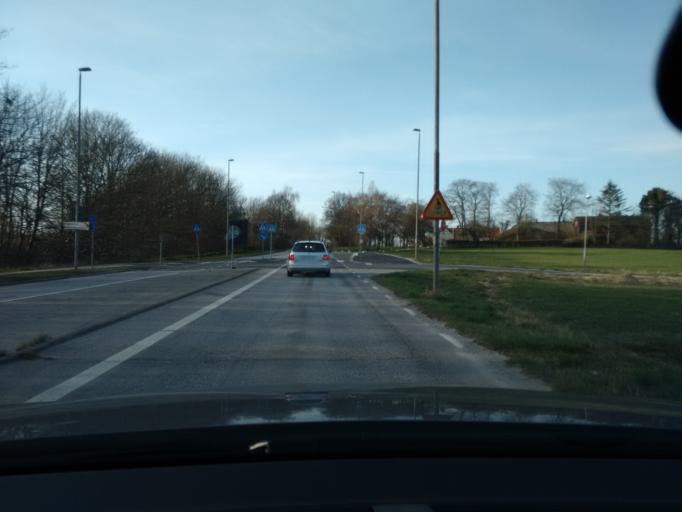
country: SE
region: Skane
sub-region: Lunds Kommun
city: Lund
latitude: 55.7292
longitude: 13.1783
